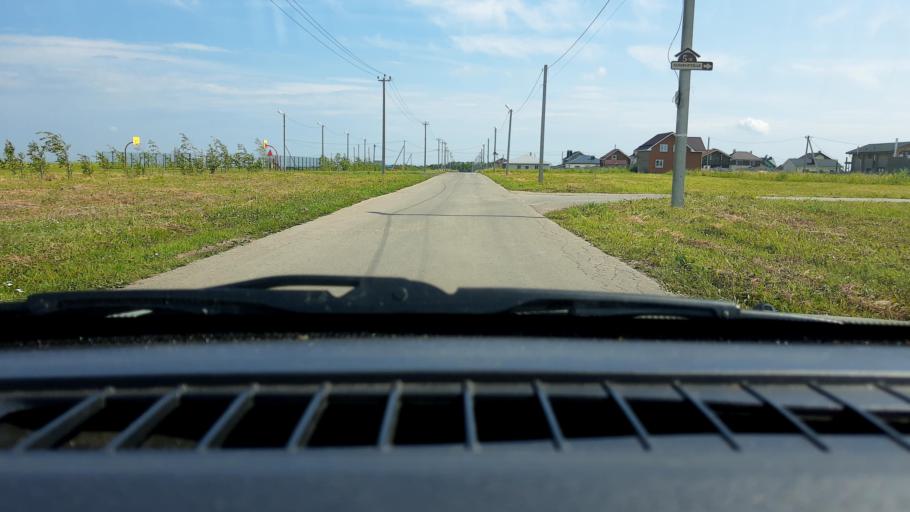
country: RU
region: Nizjnij Novgorod
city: Burevestnik
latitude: 56.1474
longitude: 43.7246
